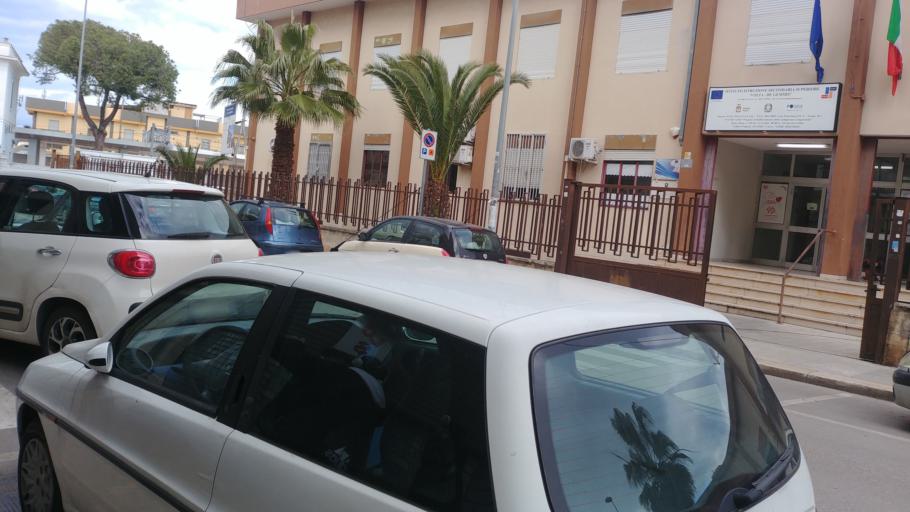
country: IT
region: Apulia
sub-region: Provincia di Bari
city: Bitonto
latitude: 41.1127
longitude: 16.6853
